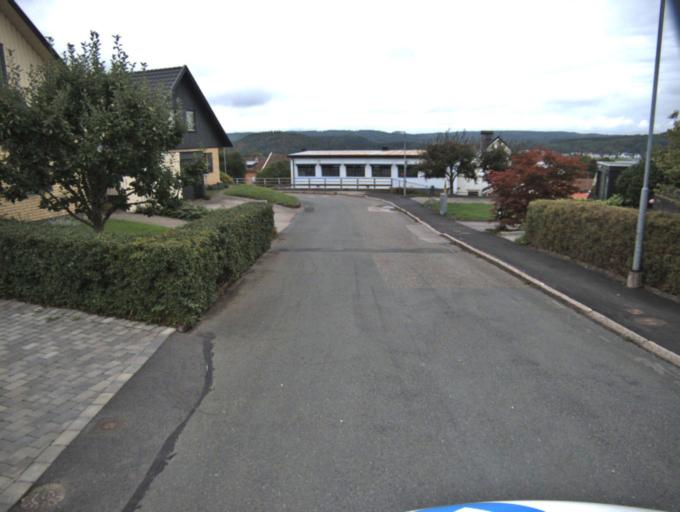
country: SE
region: Vaestra Goetaland
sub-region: Ulricehamns Kommun
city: Ulricehamn
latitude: 57.7911
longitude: 13.4199
